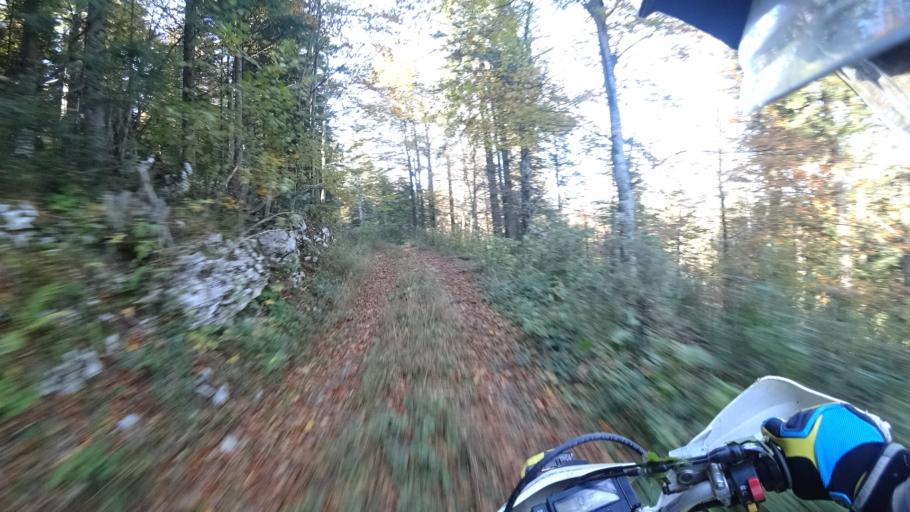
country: HR
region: Karlovacka
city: Plaski
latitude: 45.0339
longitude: 15.3488
